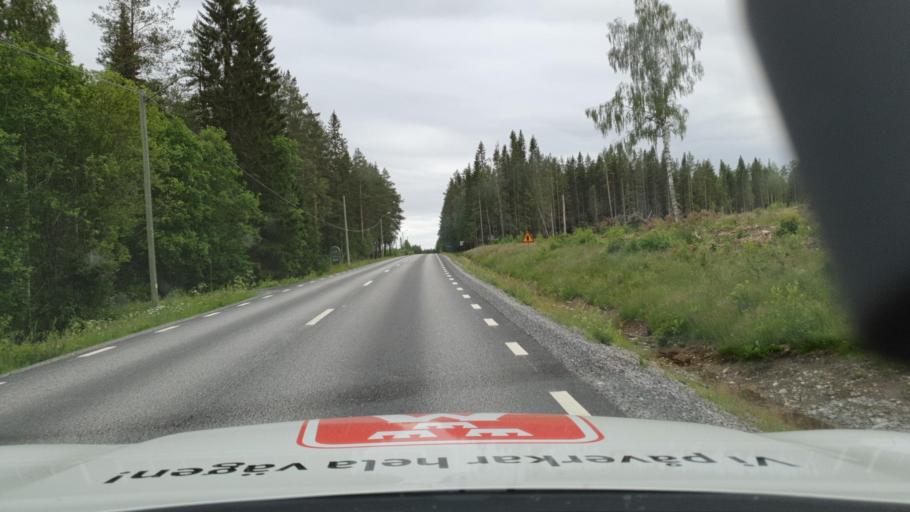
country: SE
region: Vaesterbotten
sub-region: Vannas Kommun
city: Vaennaes
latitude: 63.7344
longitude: 19.6531
